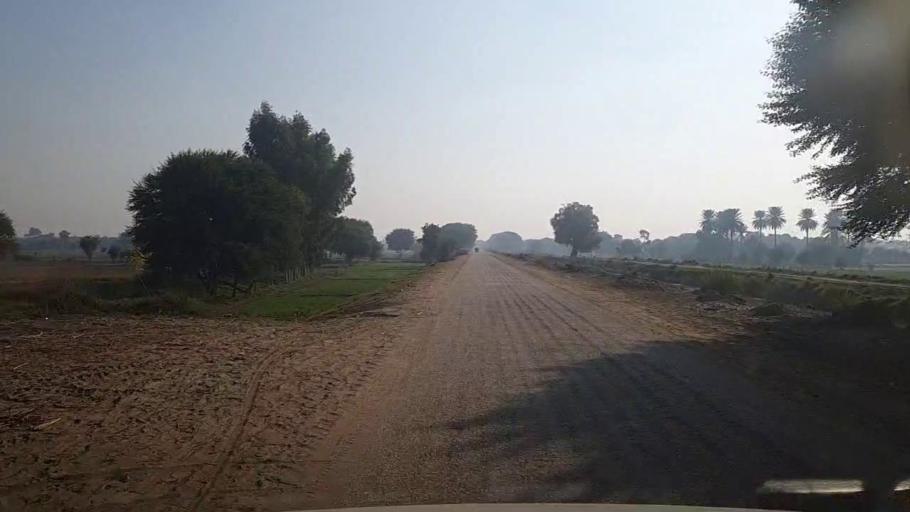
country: PK
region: Sindh
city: Kandiari
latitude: 26.8446
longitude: 68.4895
